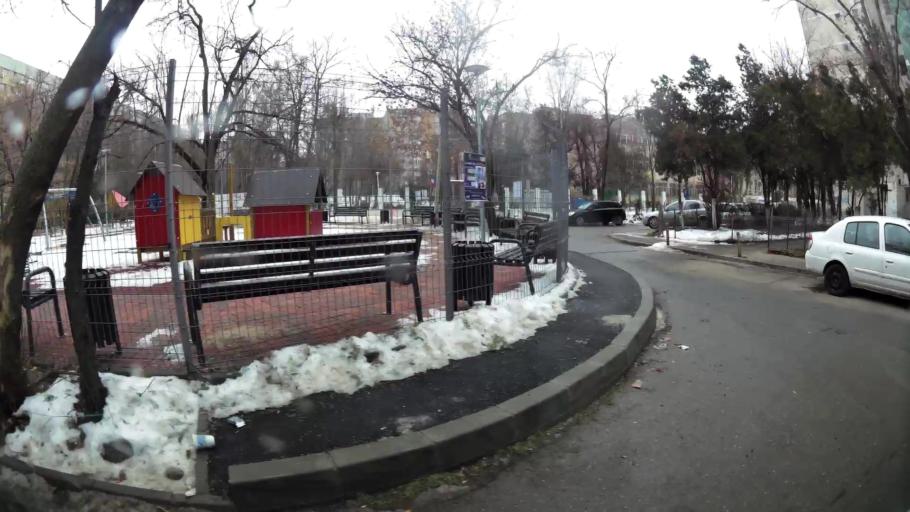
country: RO
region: Ilfov
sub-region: Comuna Chiajna
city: Rosu
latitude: 44.4228
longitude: 26.0430
